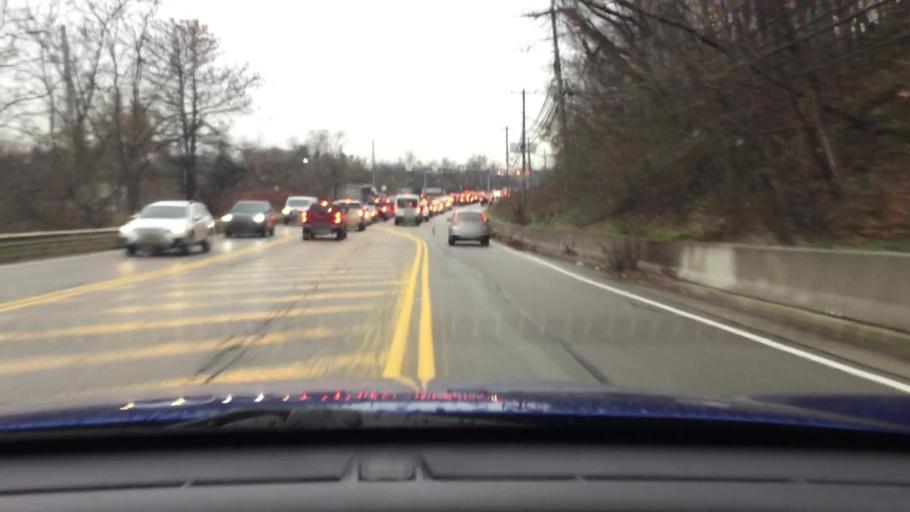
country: US
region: Pennsylvania
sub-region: Washington County
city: Canonsburg
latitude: 40.2687
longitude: -80.1619
